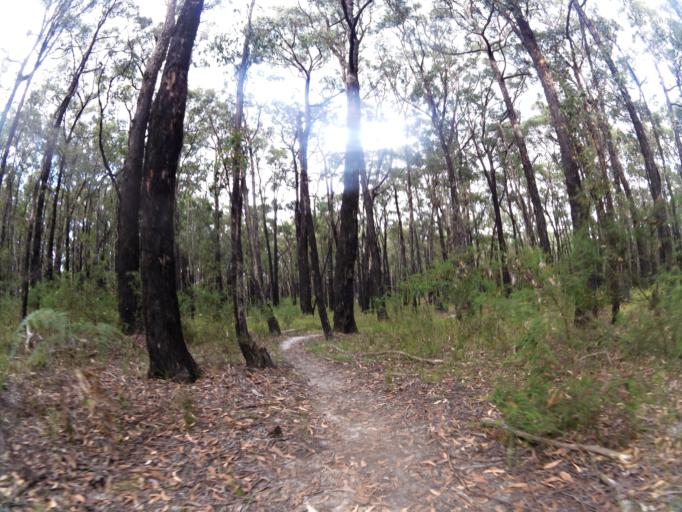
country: AU
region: Victoria
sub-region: Colac-Otway
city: Colac
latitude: -38.4976
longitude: 143.7113
